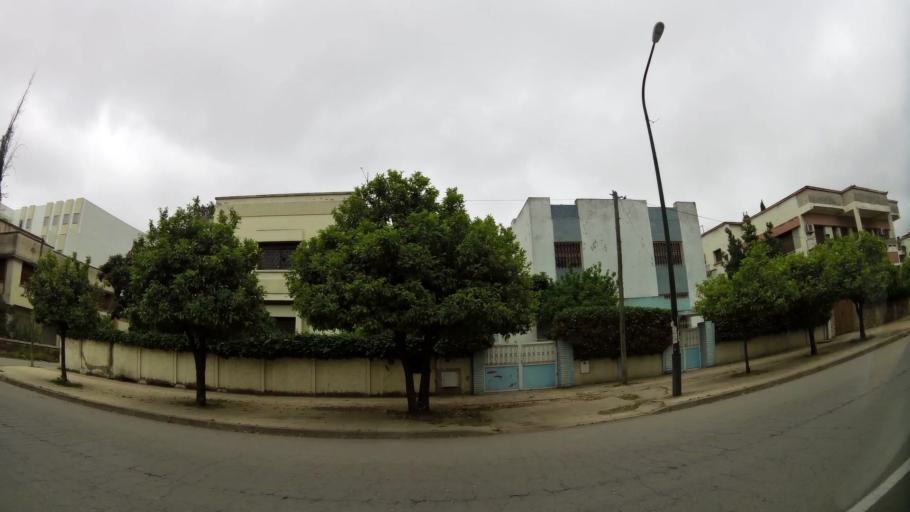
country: MA
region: Fes-Boulemane
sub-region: Fes
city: Fes
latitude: 34.0339
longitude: -5.0113
